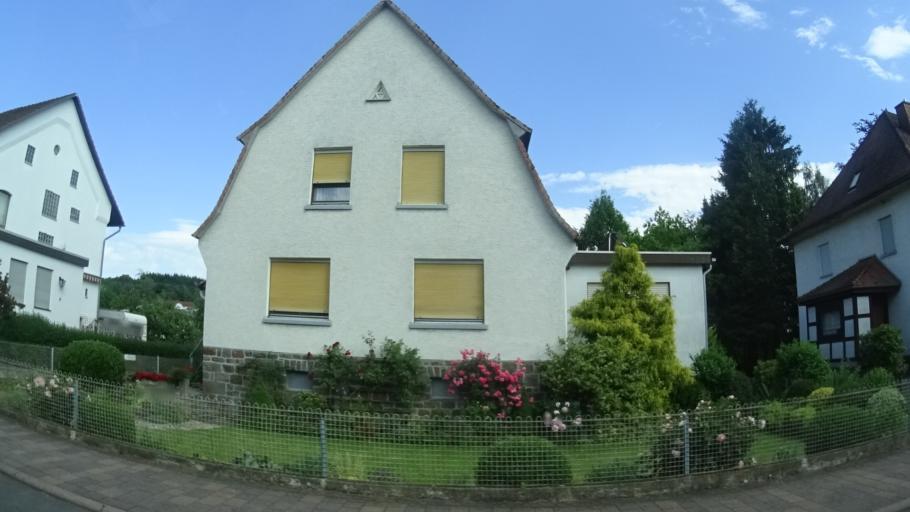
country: DE
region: Hesse
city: Haina
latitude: 51.0258
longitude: 8.9713
